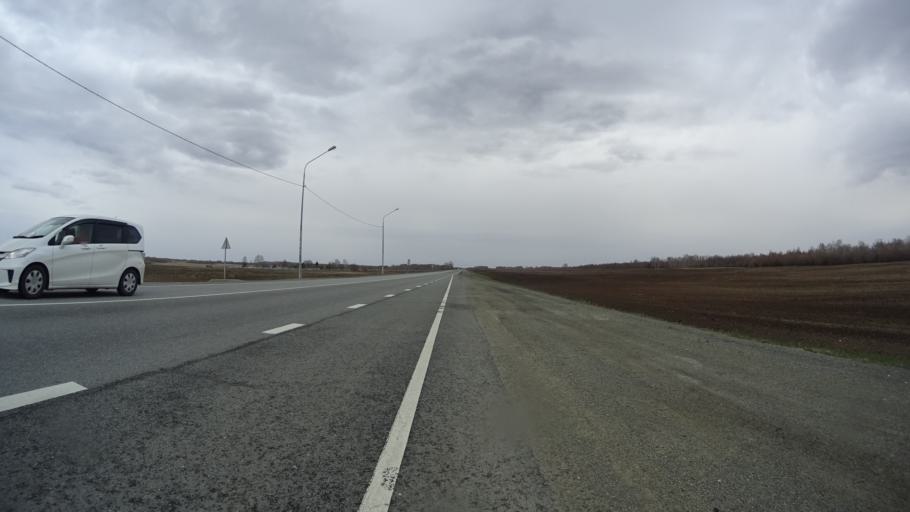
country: RU
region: Chelyabinsk
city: Krasnogorskiy
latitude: 54.6712
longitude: 61.2504
